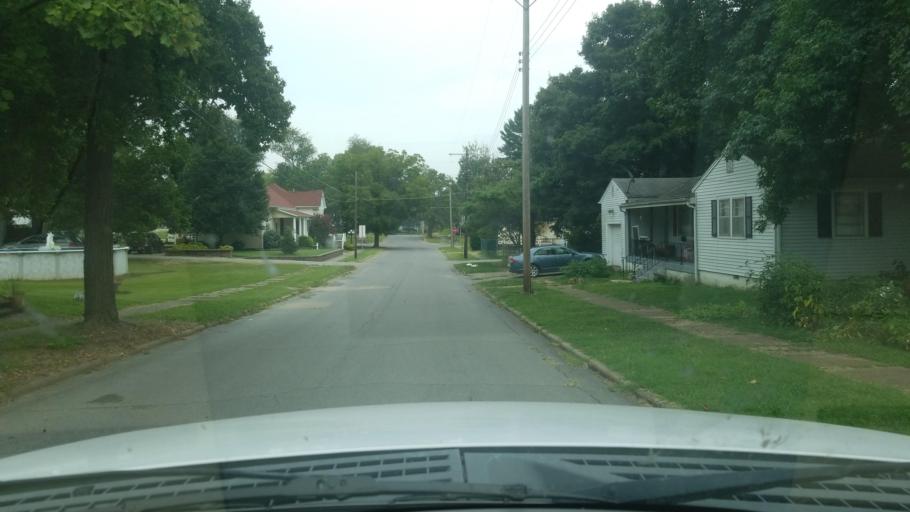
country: US
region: Illinois
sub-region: Saline County
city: Eldorado
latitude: 37.8176
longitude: -88.4443
